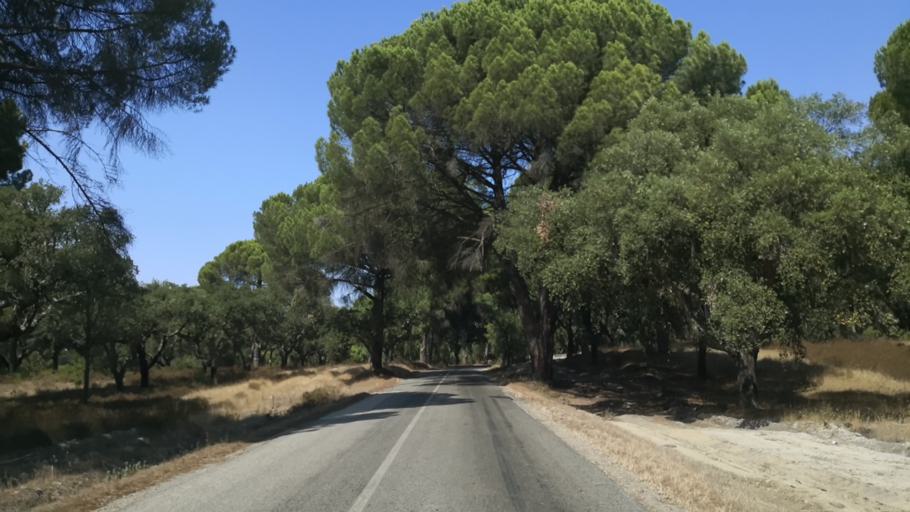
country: PT
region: Santarem
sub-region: Benavente
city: Poceirao
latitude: 38.7353
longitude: -8.6990
